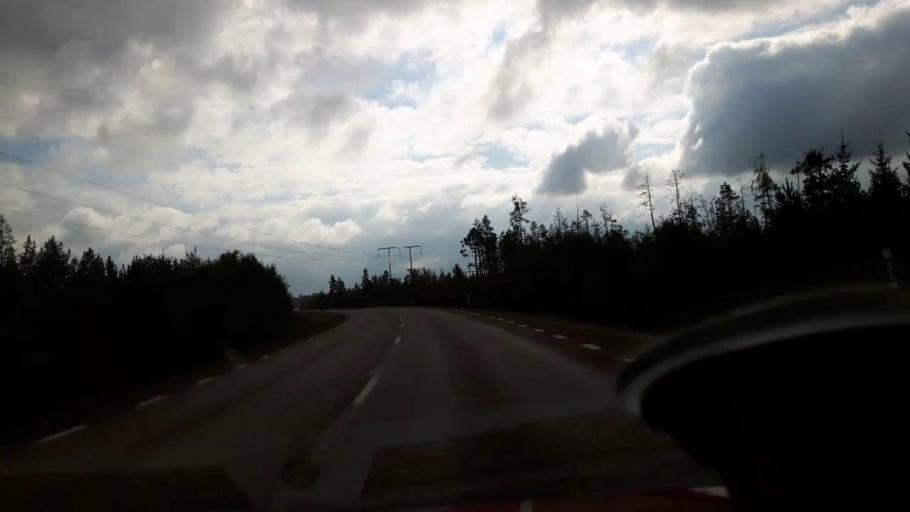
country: SE
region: Gaevleborg
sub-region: Soderhamns Kommun
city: Ljusne
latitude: 61.0907
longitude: 16.9545
